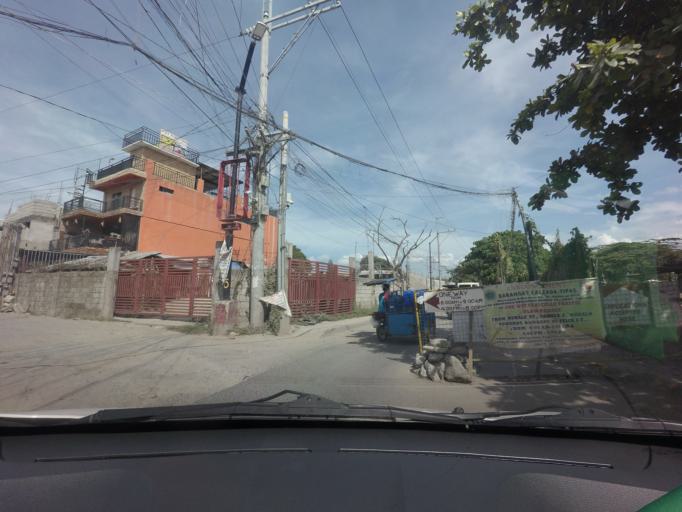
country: PH
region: Calabarzon
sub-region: Province of Rizal
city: Taguig
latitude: 14.5293
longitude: 121.0843
